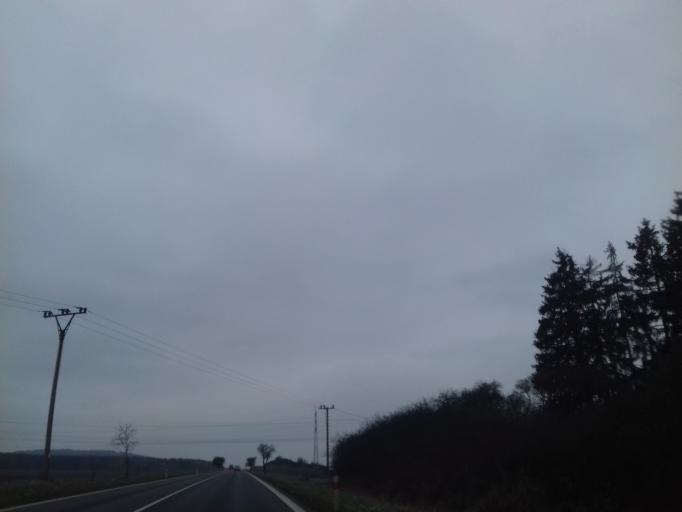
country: CZ
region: Plzensky
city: Stod
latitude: 49.6269
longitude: 13.1507
